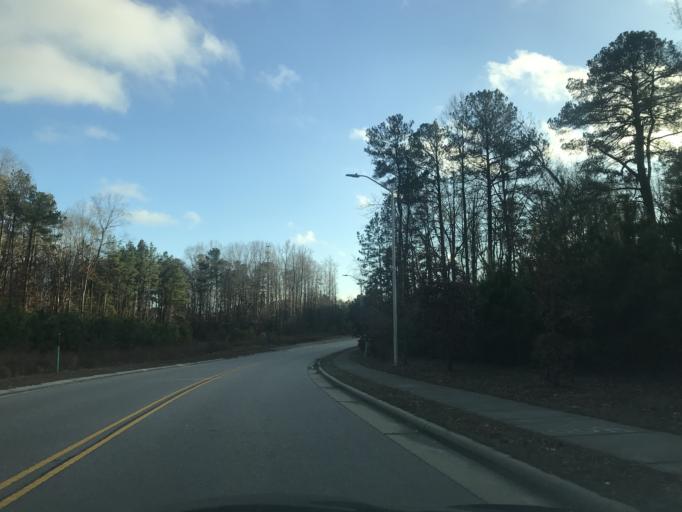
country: US
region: North Carolina
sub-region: Wake County
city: Wake Forest
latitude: 35.9550
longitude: -78.5335
